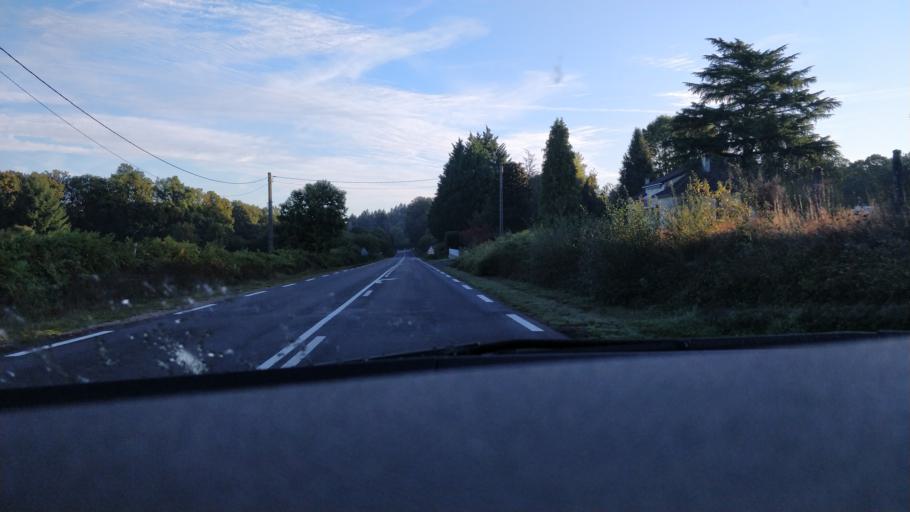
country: FR
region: Limousin
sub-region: Departement de la Haute-Vienne
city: Sauviat-sur-Vige
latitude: 45.8924
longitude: 1.5767
